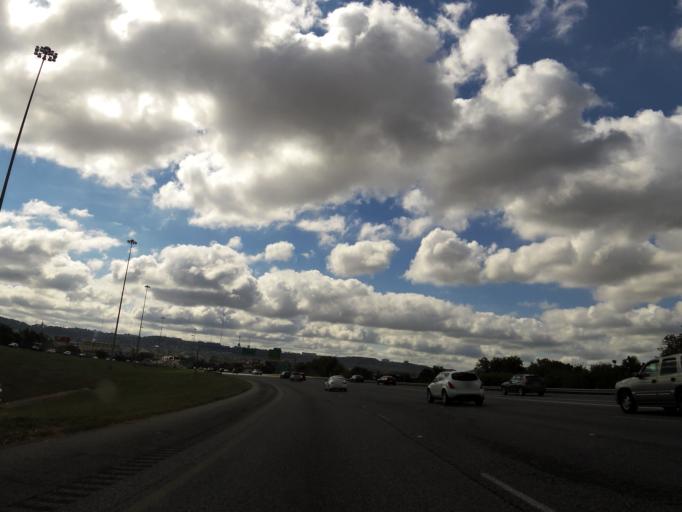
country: US
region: Alabama
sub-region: Jefferson County
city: Birmingham
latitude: 33.5183
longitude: -86.8259
